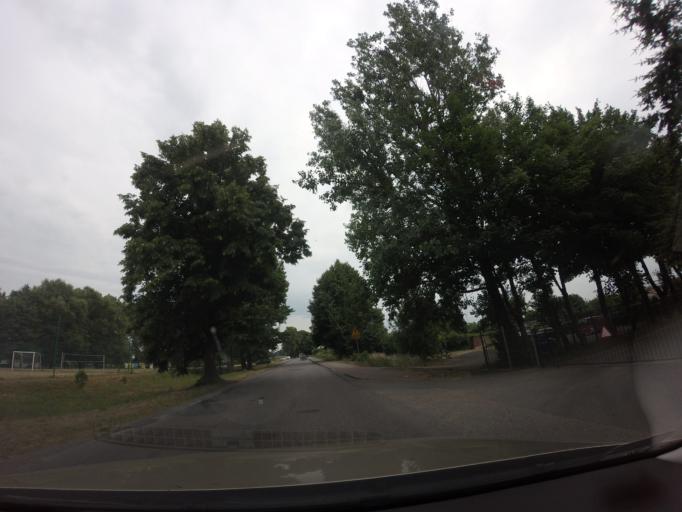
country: PL
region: West Pomeranian Voivodeship
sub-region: Powiat drawski
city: Czaplinek
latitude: 53.5469
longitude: 16.2321
